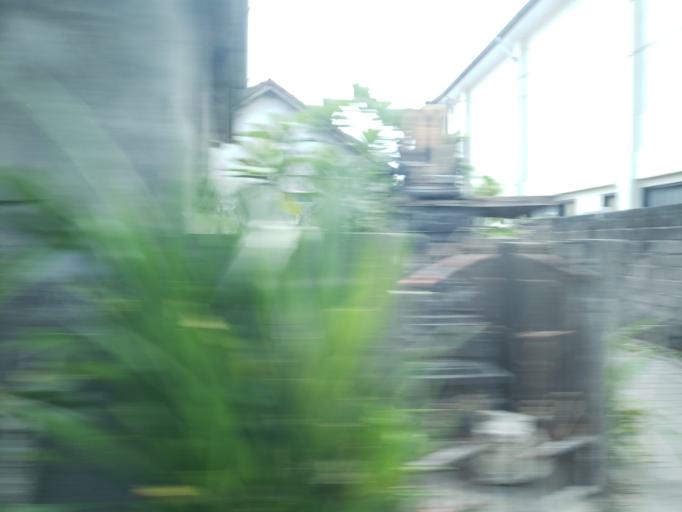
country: ID
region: Bali
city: Kangin
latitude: -8.8265
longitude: 115.1504
